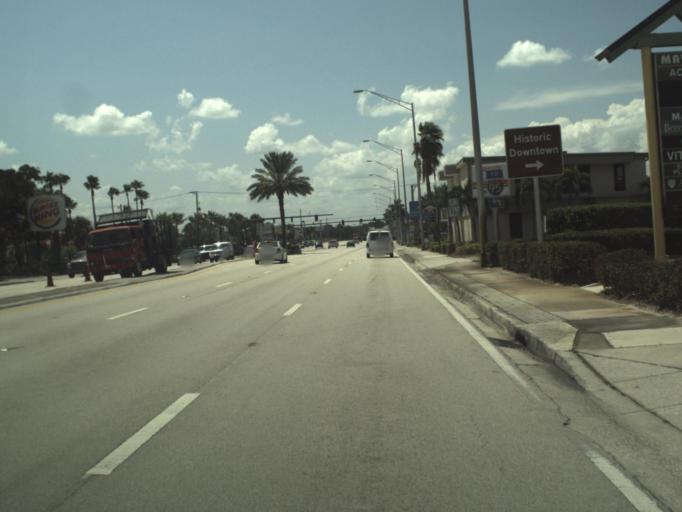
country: US
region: Florida
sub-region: Martin County
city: Stuart
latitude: 27.1903
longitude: -80.2510
